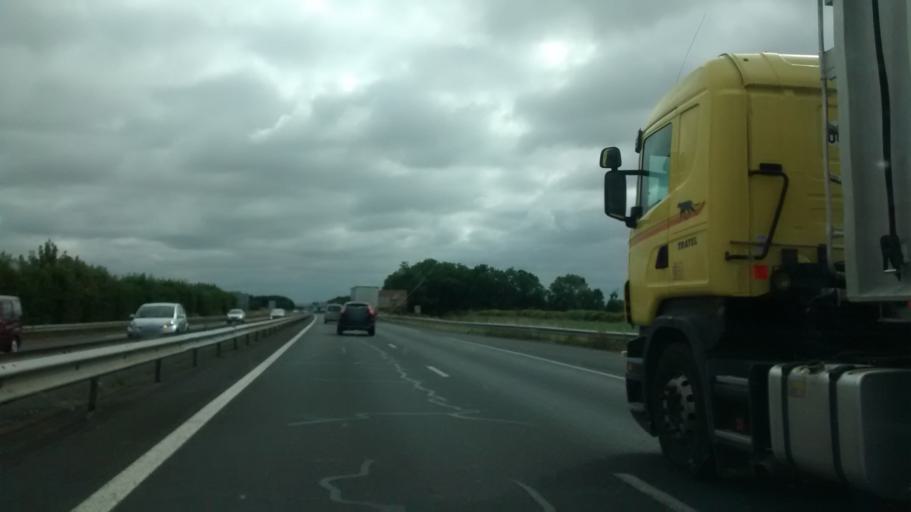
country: FR
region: Lower Normandy
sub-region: Departement du Calvados
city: Mouen
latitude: 49.1562
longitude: -0.4814
